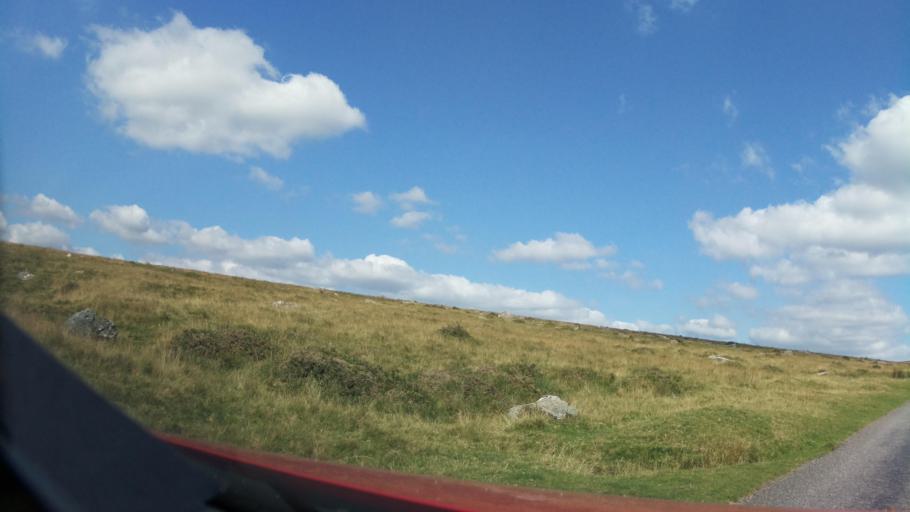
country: GB
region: England
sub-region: Devon
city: Yelverton
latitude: 50.5566
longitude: -4.0306
